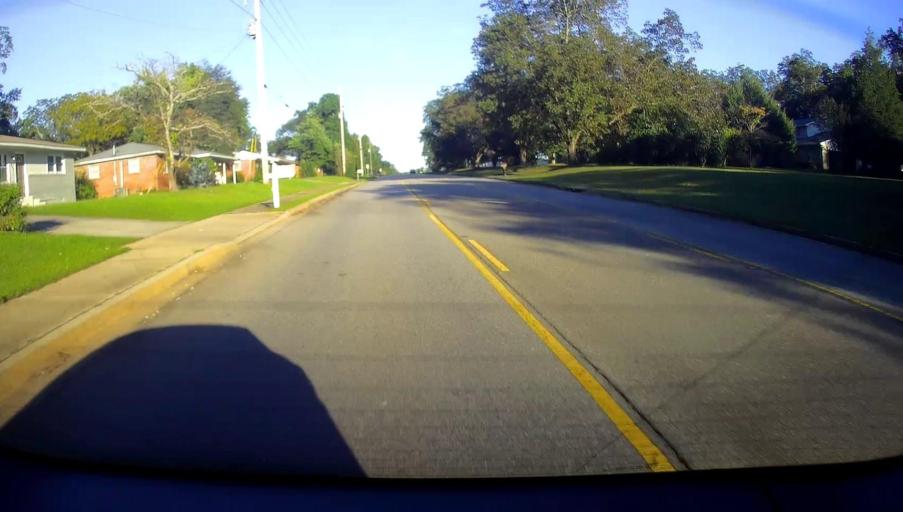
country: US
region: Georgia
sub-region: Houston County
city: Centerville
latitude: 32.6350
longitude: -83.6992
